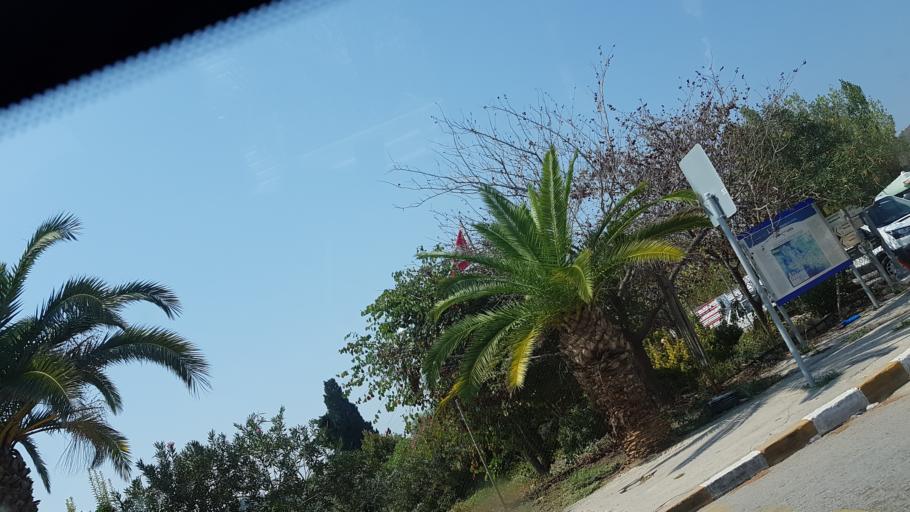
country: TR
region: Izmir
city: Urla
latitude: 38.3630
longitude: 26.7698
